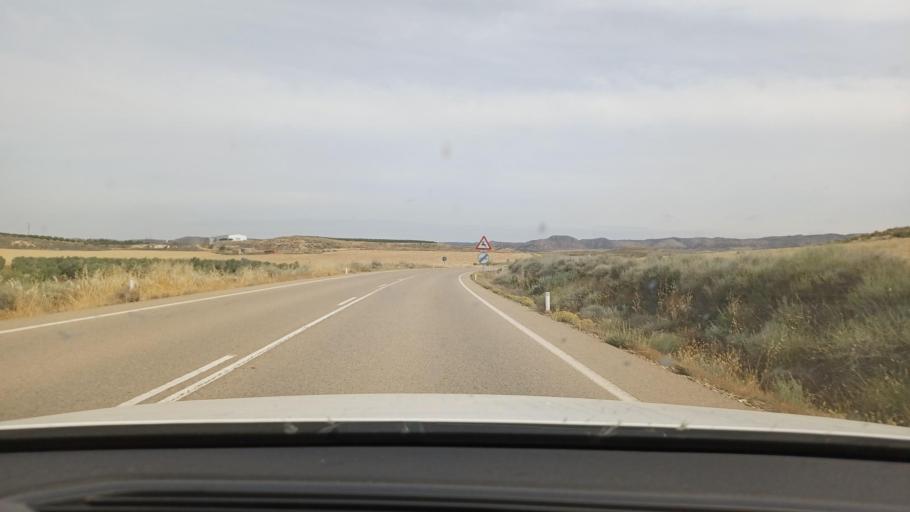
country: ES
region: Aragon
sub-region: Provincia de Zaragoza
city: Chiprana
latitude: 41.2984
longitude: -0.0670
